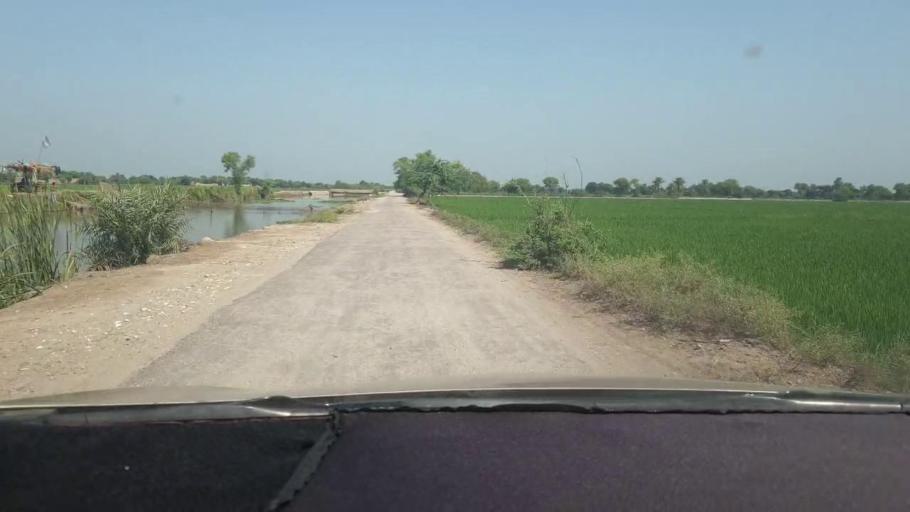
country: PK
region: Sindh
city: Miro Khan
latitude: 27.7055
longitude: 68.0750
